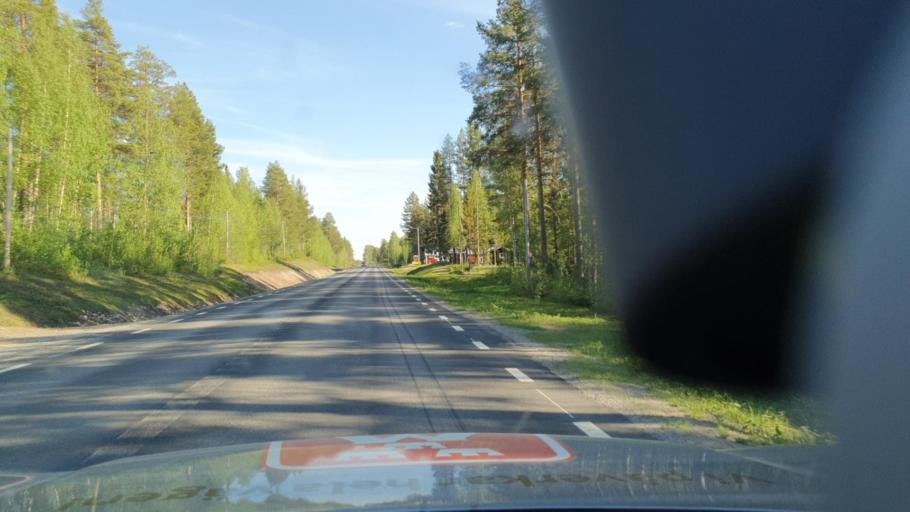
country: SE
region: Norrbotten
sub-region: Alvsbyns Kommun
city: AElvsbyn
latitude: 66.1163
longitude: 20.9260
